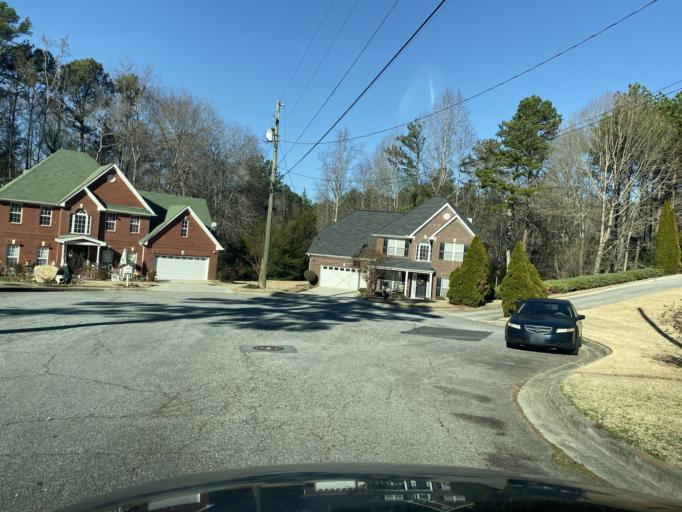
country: US
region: Georgia
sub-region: DeKalb County
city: Pine Mountain
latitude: 33.6852
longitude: -84.1588
